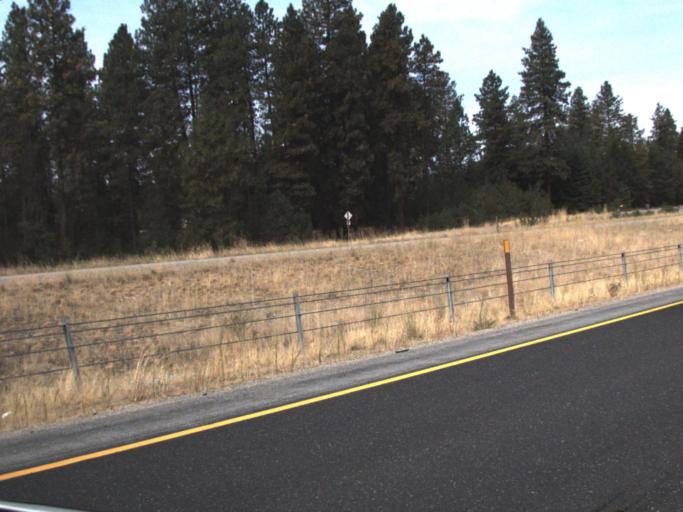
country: US
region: Washington
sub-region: Spokane County
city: Fairwood
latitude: 47.8182
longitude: -117.4110
